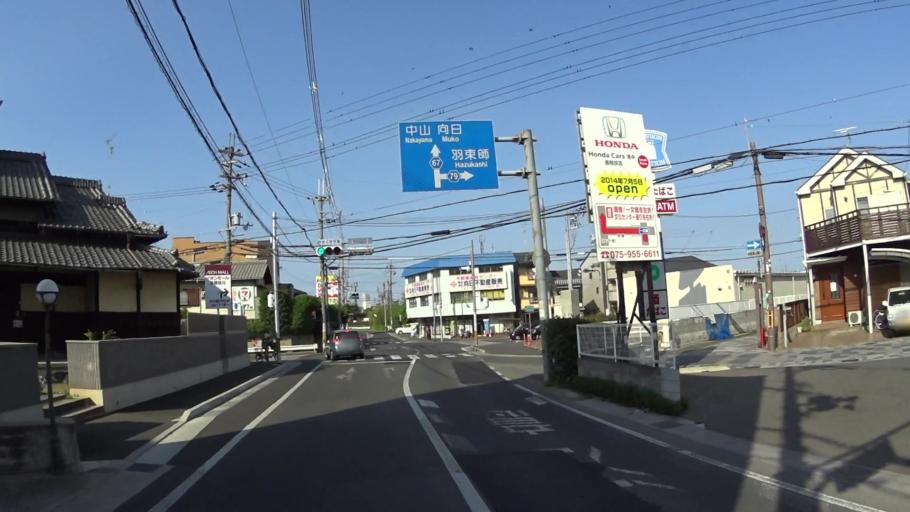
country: JP
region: Kyoto
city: Muko
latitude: 34.9289
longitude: 135.6987
